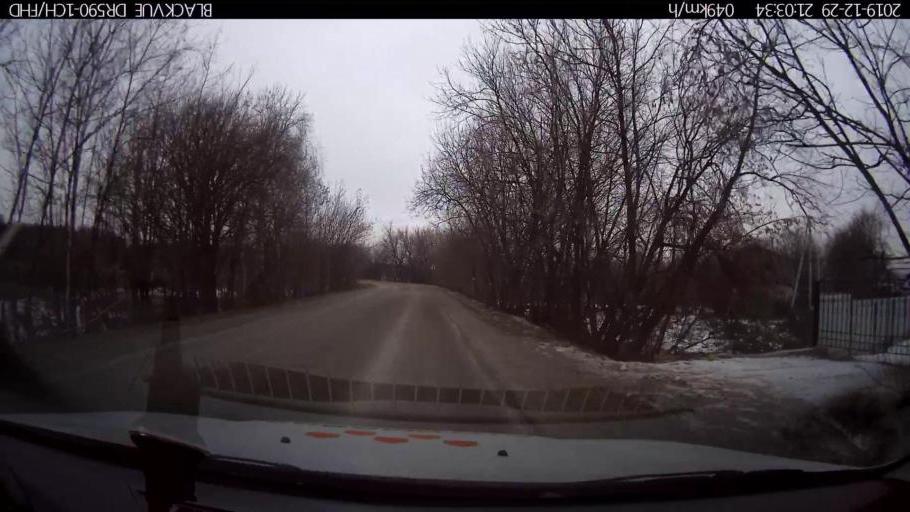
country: RU
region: Nizjnij Novgorod
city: Afonino
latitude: 56.1962
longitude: 44.0060
